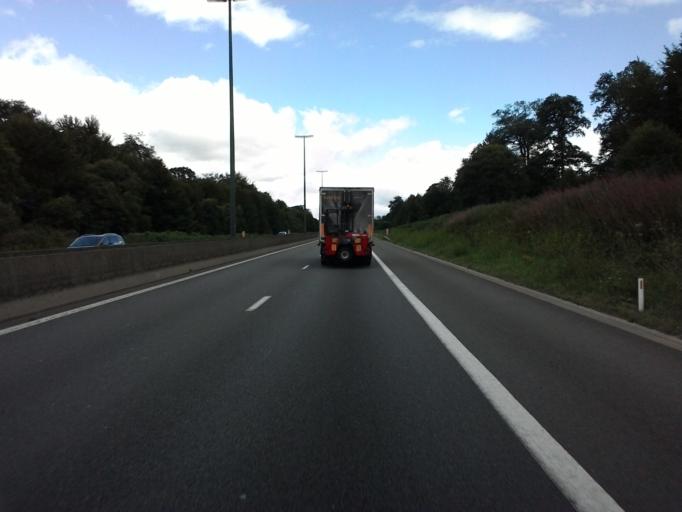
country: BE
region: Wallonia
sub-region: Province du Luxembourg
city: Habay-la-Vieille
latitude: 49.7402
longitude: 5.5742
